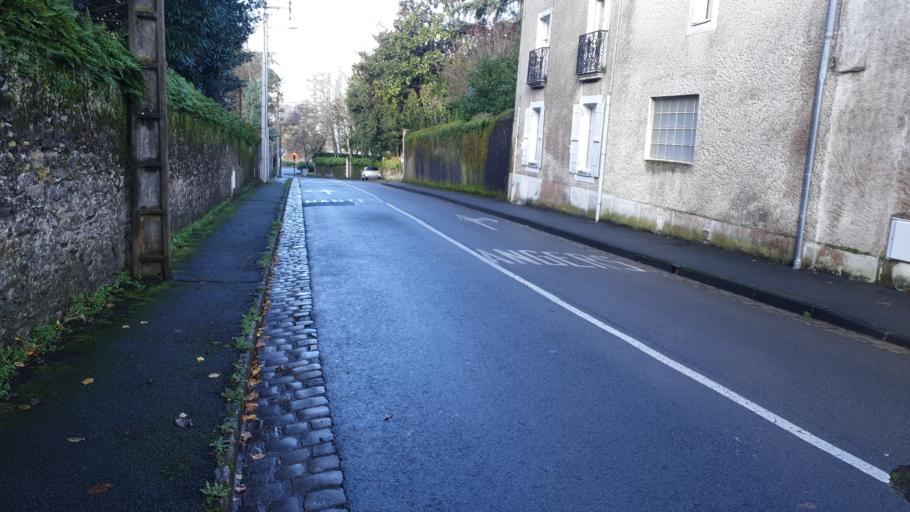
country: FR
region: Pays de la Loire
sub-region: Departement de la Loire-Atlantique
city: Saint-Sebastien-sur-Loire
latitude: 47.2015
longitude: -1.5281
